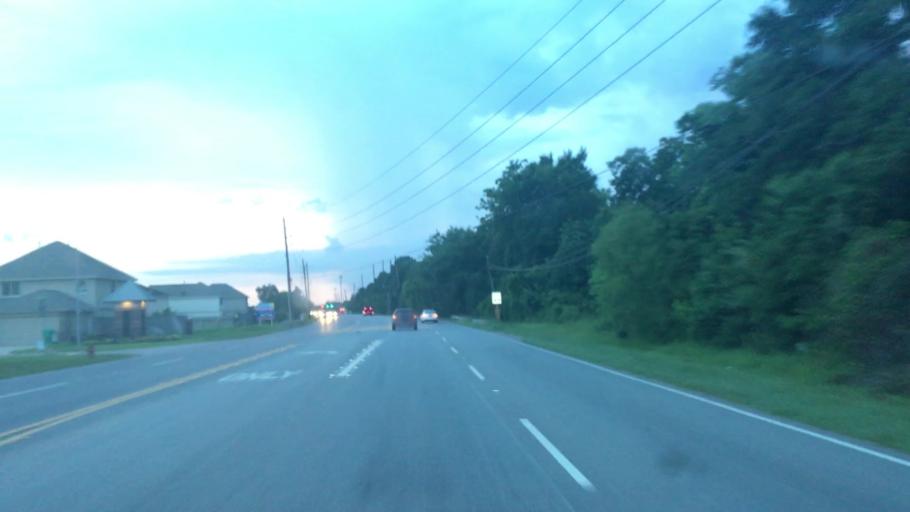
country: US
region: Texas
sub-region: Harris County
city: Humble
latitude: 29.9732
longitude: -95.2288
